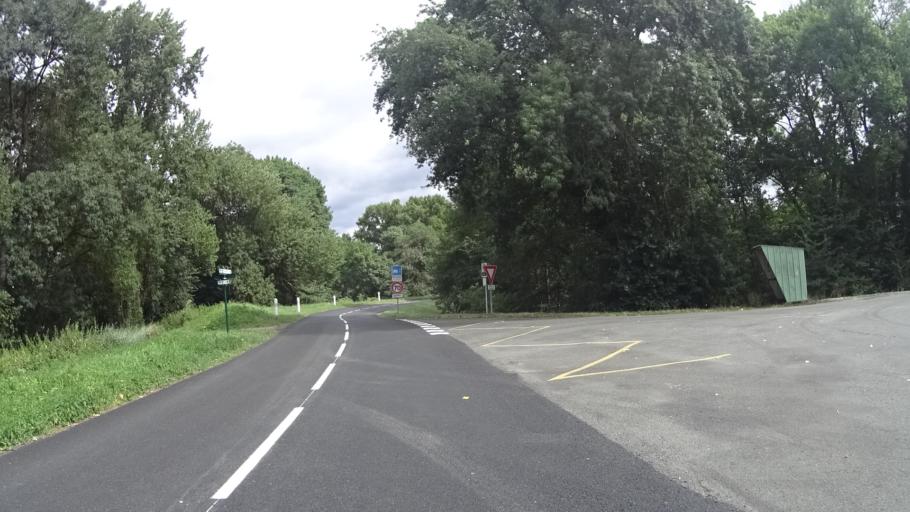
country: FR
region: Centre
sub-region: Departement d'Indre-et-Loire
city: Huismes
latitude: 47.2736
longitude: 0.3207
